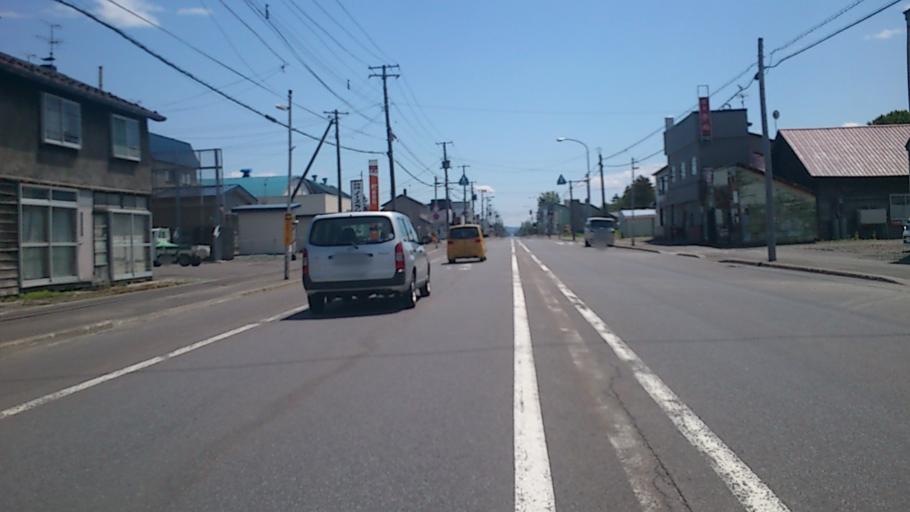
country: JP
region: Hokkaido
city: Nayoro
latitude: 44.2429
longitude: 142.3949
